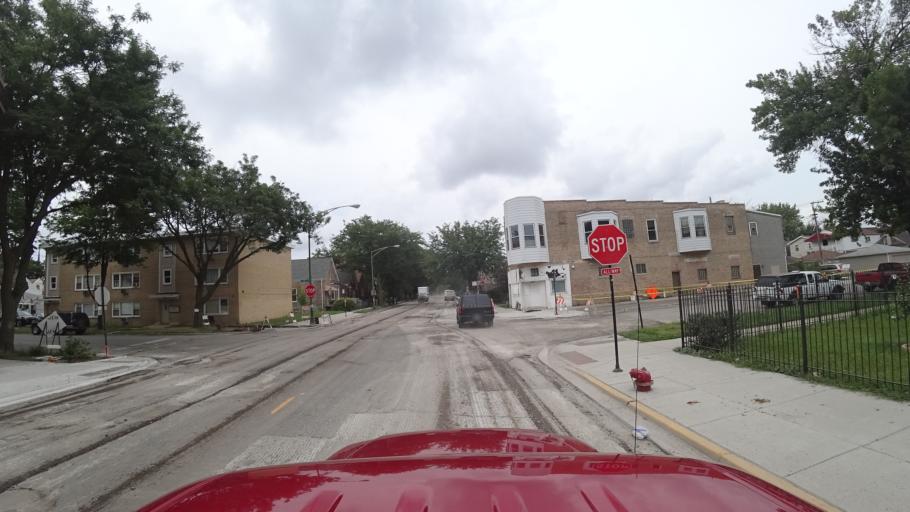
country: US
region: Illinois
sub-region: Cook County
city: Chicago
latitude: 41.8287
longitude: -87.6753
